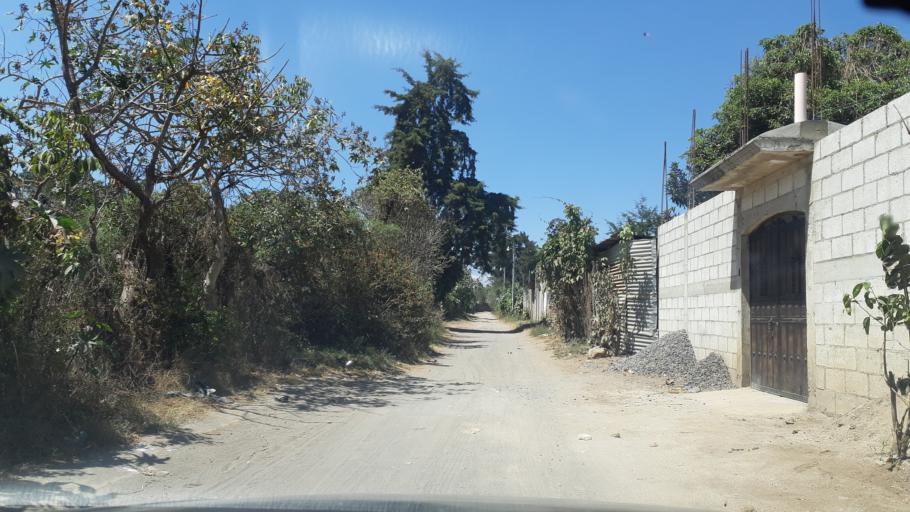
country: GT
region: Chimaltenango
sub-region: Municipio de Chimaltenango
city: Chimaltenango
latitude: 14.6483
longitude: -90.8101
